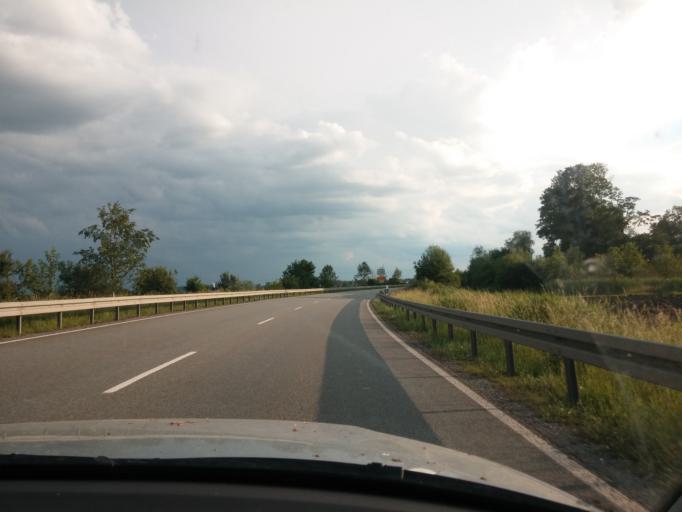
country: DE
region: Bavaria
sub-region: Upper Bavaria
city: Ebersberg
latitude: 48.0641
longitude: 11.9768
